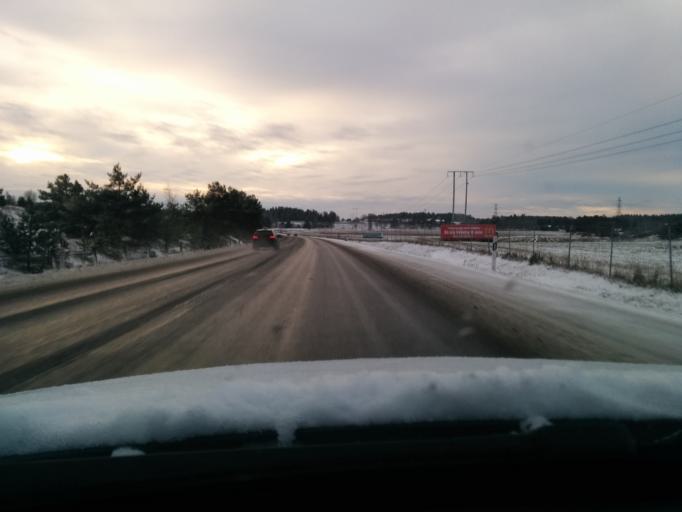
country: SE
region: Stockholm
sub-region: Sigtuna Kommun
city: Marsta
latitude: 59.6816
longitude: 17.8688
